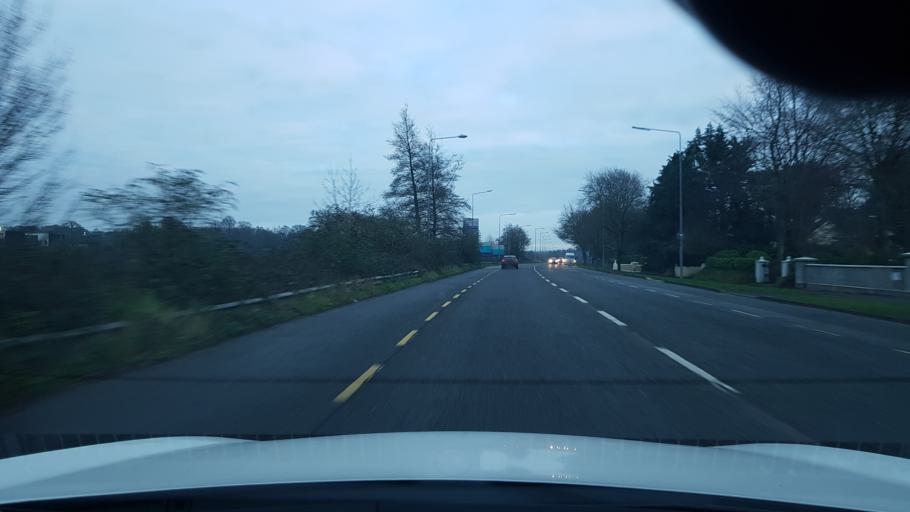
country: IE
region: Leinster
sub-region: An Mhi
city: Navan
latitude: 53.6387
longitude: -6.6674
